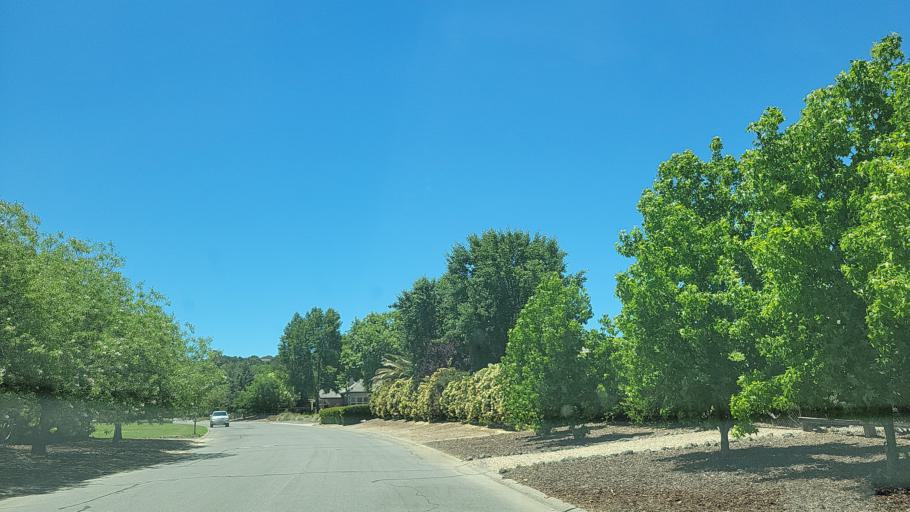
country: US
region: California
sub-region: San Luis Obispo County
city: Atascadero
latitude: 35.5166
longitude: -120.6745
